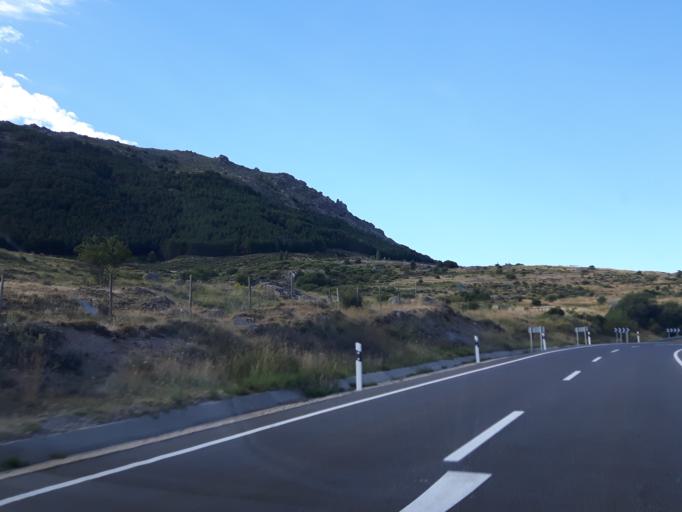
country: ES
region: Castille and Leon
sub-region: Provincia de Avila
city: Mengamunoz
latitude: 40.4921
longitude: -5.0059
